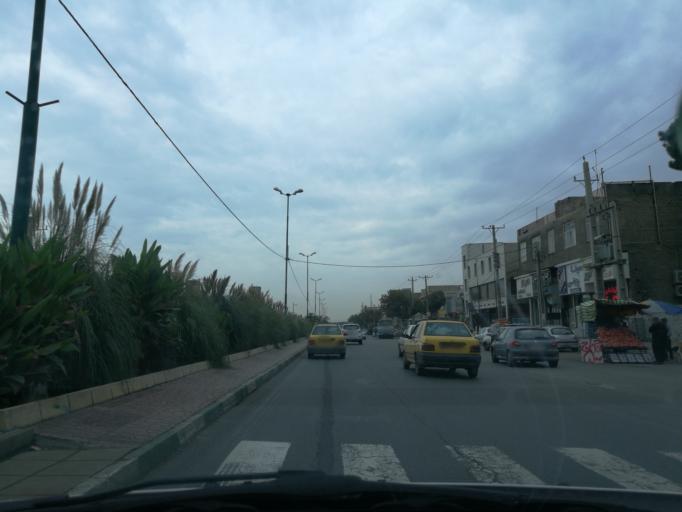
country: IR
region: Alborz
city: Karaj
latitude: 35.8457
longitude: 50.9188
